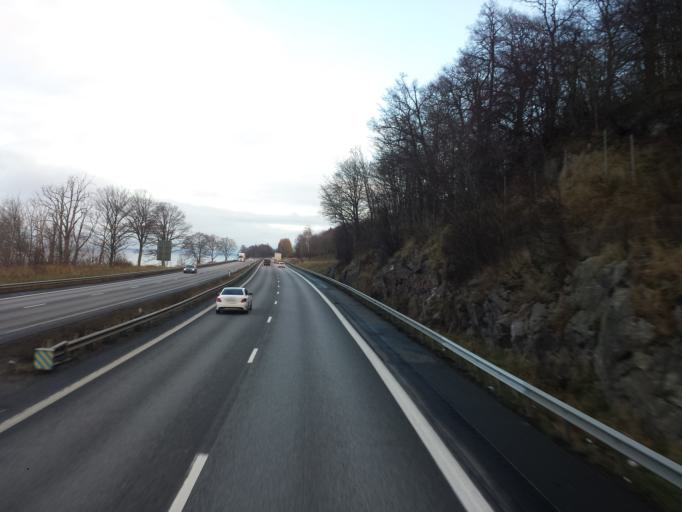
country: SE
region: Joenkoeping
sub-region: Jonkopings Kommun
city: Kaxholmen
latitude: 57.8732
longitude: 14.2745
